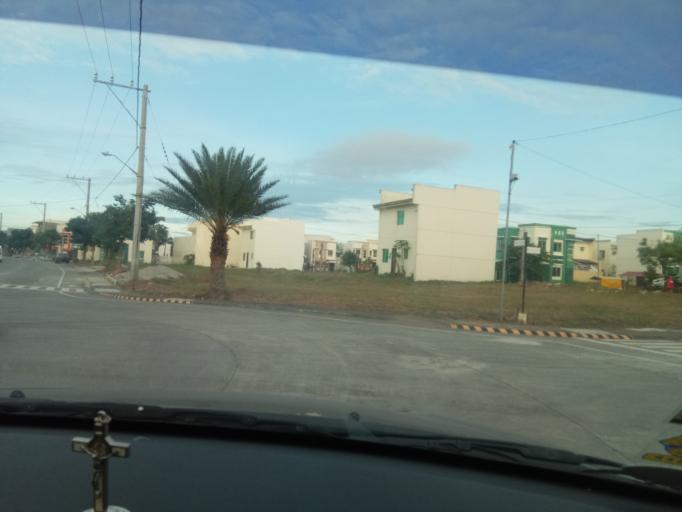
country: PH
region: Calabarzon
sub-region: Province of Cavite
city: Biga
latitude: 14.2756
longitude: 120.9677
